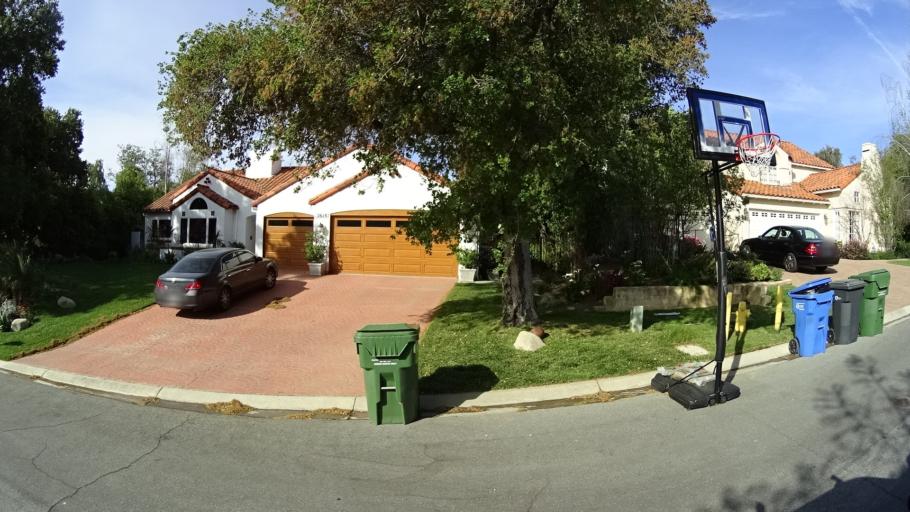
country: US
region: California
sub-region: Ventura County
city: Oak Park
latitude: 34.1954
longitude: -118.7910
